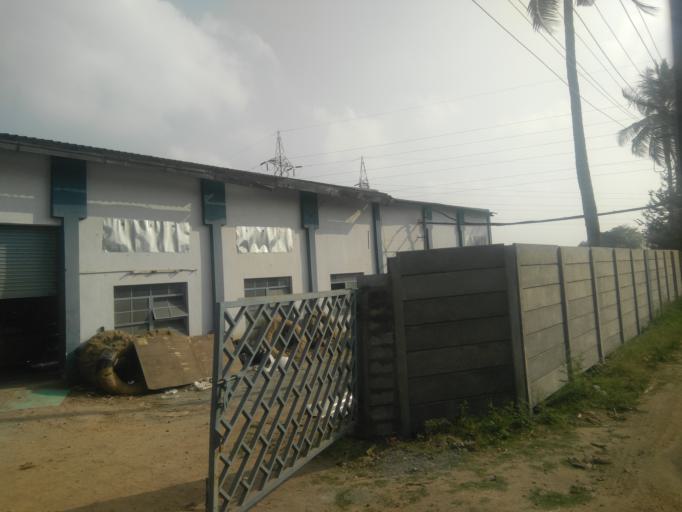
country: IN
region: Tamil Nadu
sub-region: Coimbatore
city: Periyanayakkanpalaiyam
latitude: 11.0788
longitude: 76.9355
